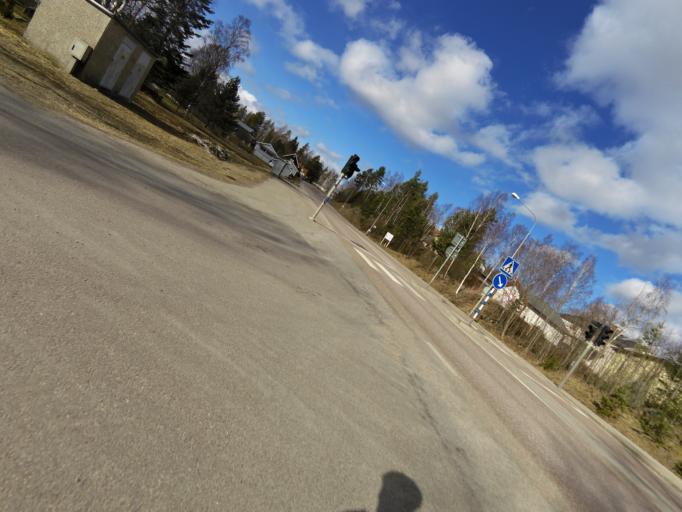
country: SE
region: Gaevleborg
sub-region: Hofors Kommun
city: Hofors
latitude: 60.5380
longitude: 16.2975
